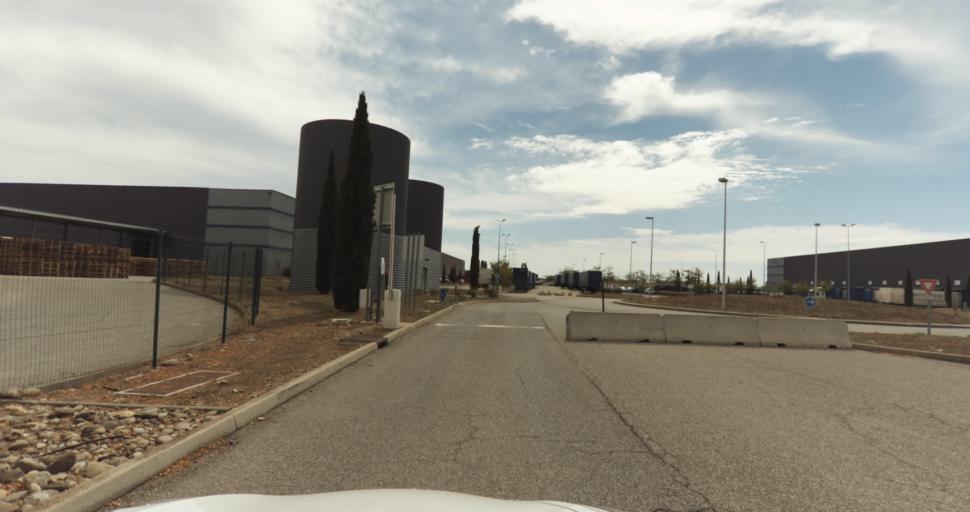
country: FR
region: Provence-Alpes-Cote d'Azur
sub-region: Departement des Bouches-du-Rhone
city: Miramas
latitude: 43.6028
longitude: 4.9938
